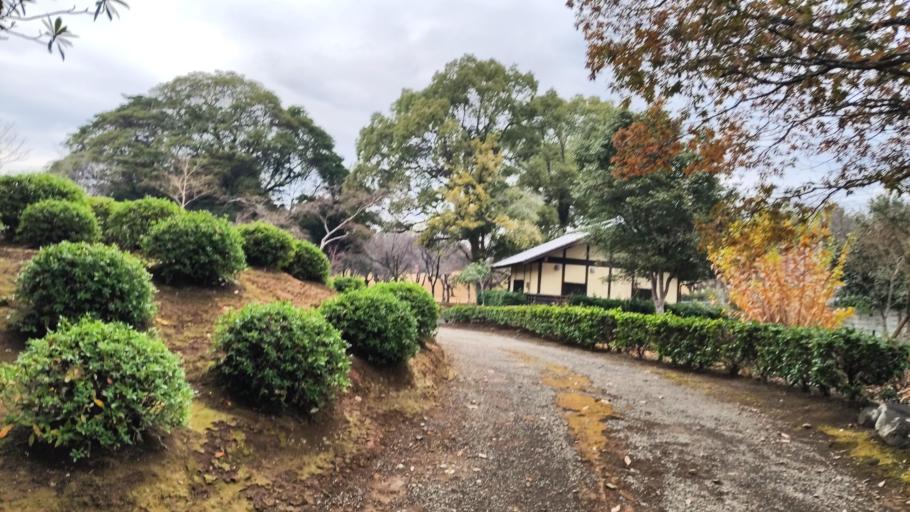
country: JP
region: Kumamoto
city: Kumamoto
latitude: 32.7900
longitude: 130.7351
